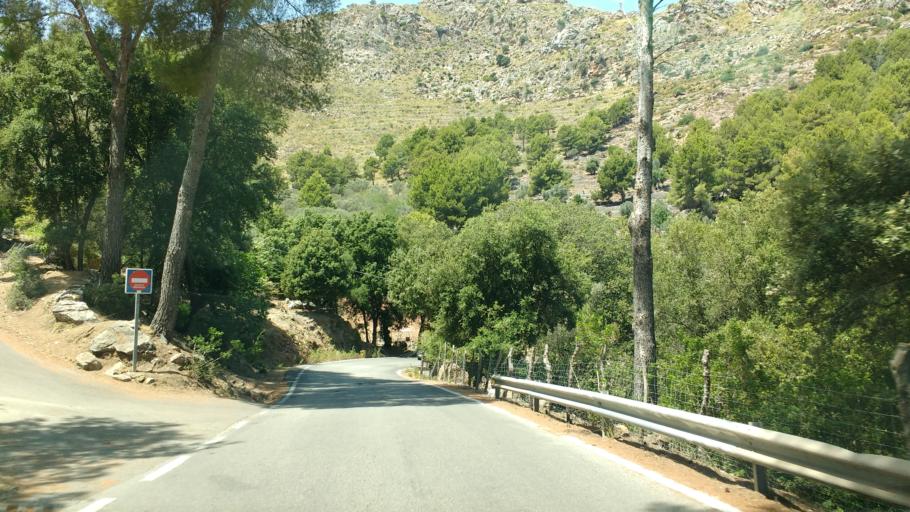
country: ES
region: Balearic Islands
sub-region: Illes Balears
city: Escorca
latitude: 39.8444
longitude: 2.7949
